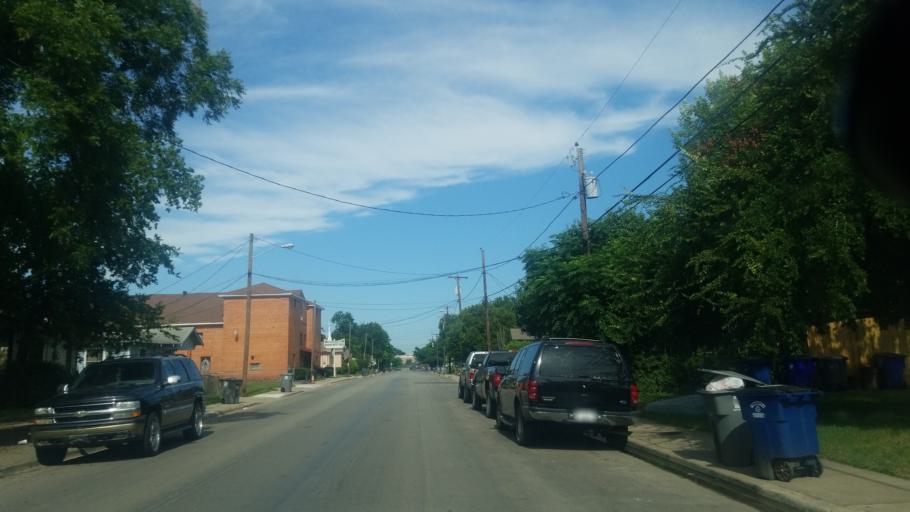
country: US
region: Texas
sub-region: Dallas County
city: Dallas
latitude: 32.7818
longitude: -96.8507
